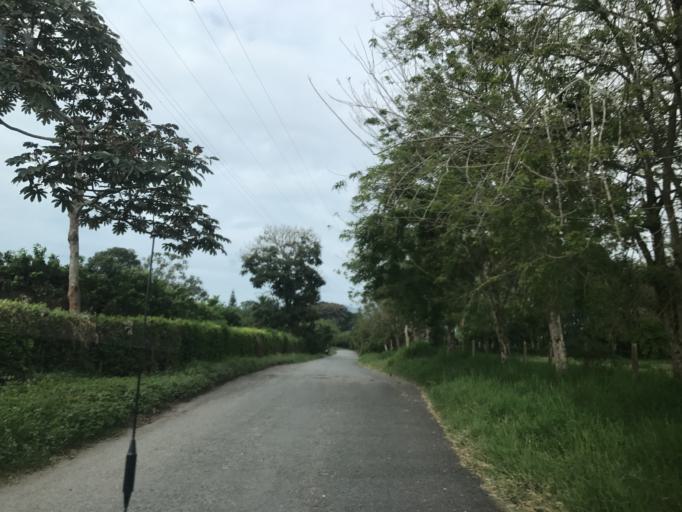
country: CO
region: Quindio
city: Montenegro
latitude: 4.5412
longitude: -75.8511
